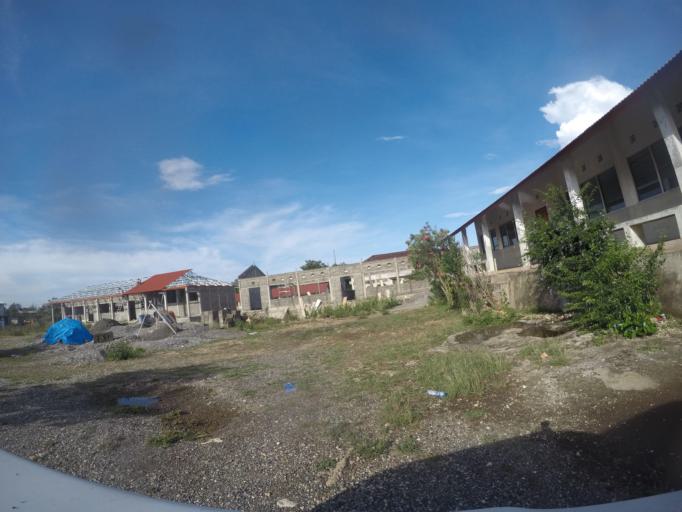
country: TL
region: Baucau
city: Baucau
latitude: -8.4872
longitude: 126.4563
